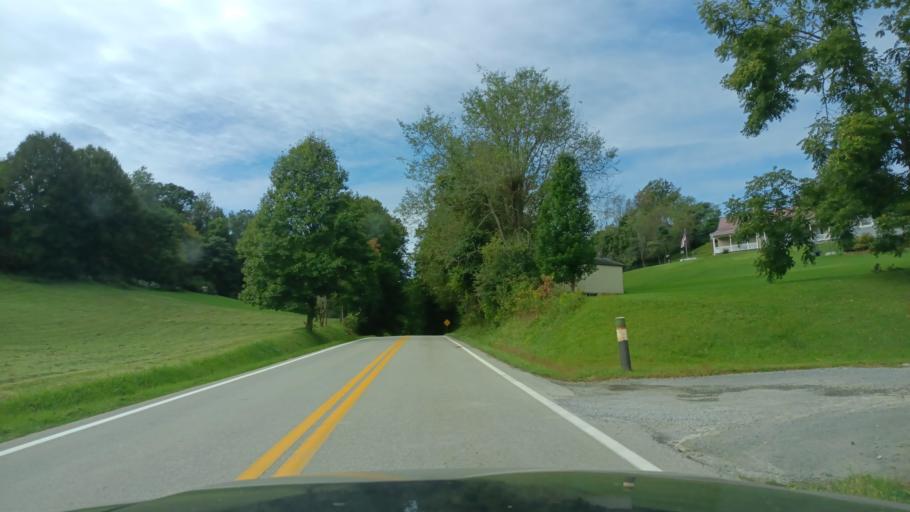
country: US
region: West Virginia
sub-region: Harrison County
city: Bridgeport
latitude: 39.3037
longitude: -80.1615
